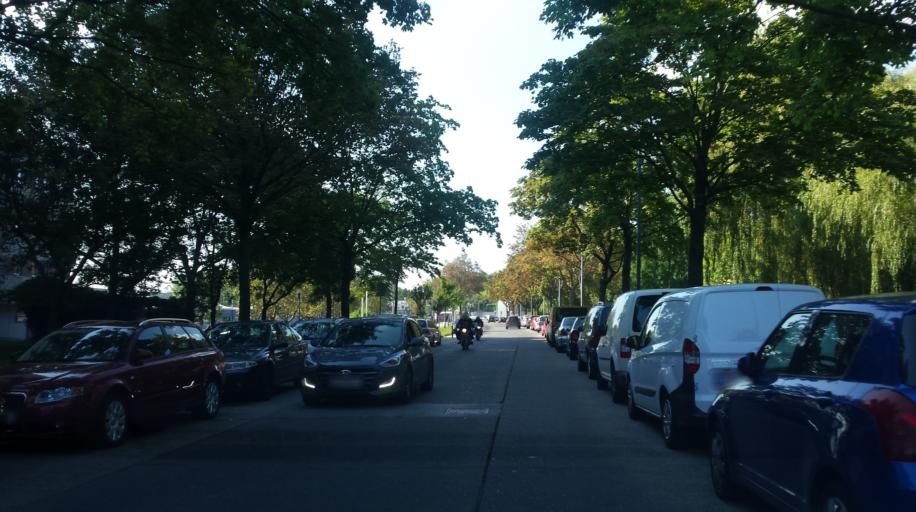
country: AT
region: Lower Austria
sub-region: Politischer Bezirk Wien-Umgebung
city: Leopoldsdorf
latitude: 48.1530
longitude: 16.3855
